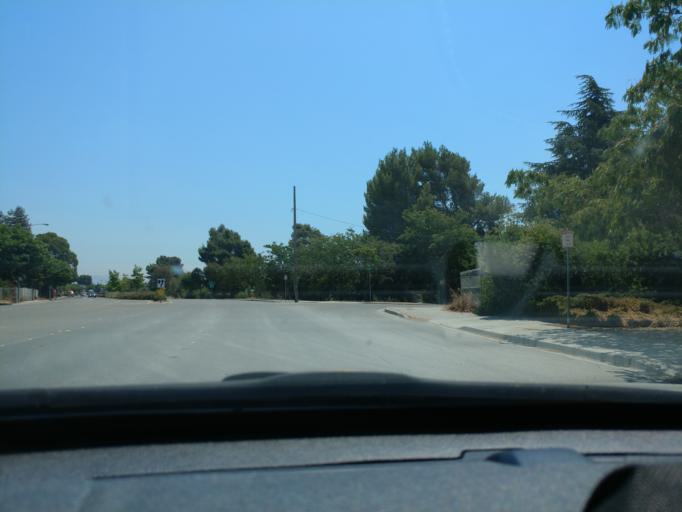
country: US
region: California
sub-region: Santa Clara County
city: Milpitas
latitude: 37.4465
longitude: -121.9090
